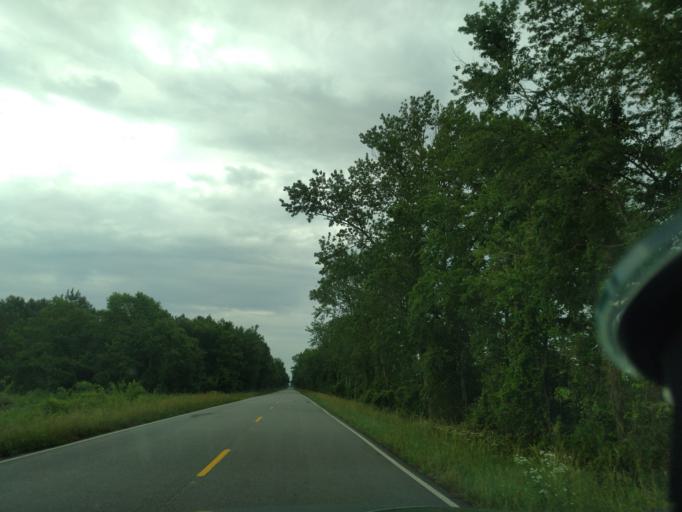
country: US
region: North Carolina
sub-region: Washington County
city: Plymouth
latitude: 35.8589
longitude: -76.5757
